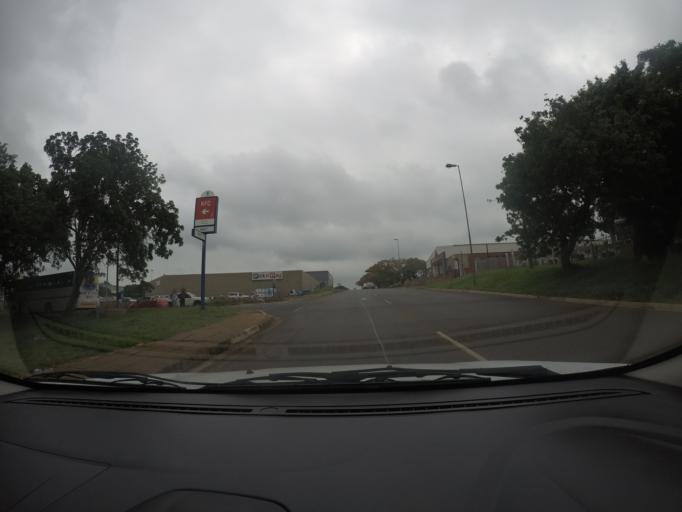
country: ZA
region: KwaZulu-Natal
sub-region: uThungulu District Municipality
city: Empangeni
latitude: -28.7390
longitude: 31.8912
